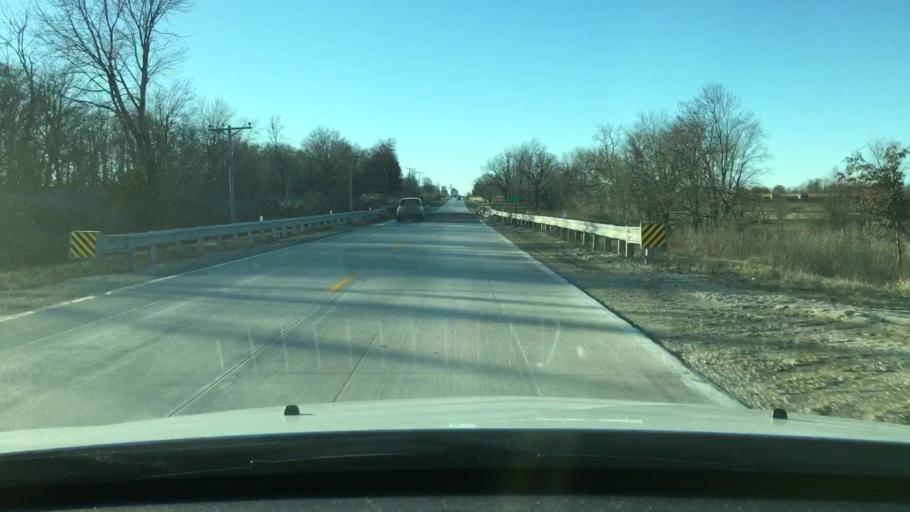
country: US
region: Missouri
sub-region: Boone County
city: Centralia
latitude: 39.2078
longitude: -92.1034
